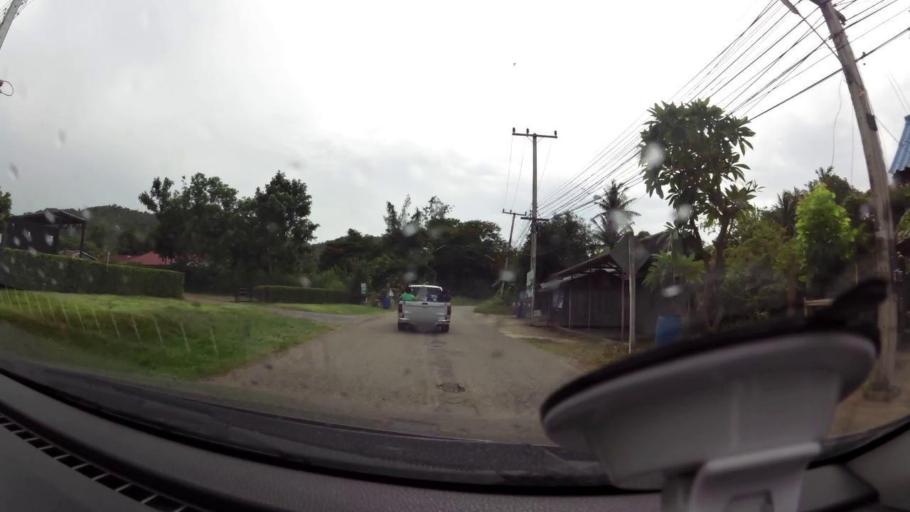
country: TH
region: Prachuap Khiri Khan
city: Pran Buri
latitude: 12.4350
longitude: 99.9756
